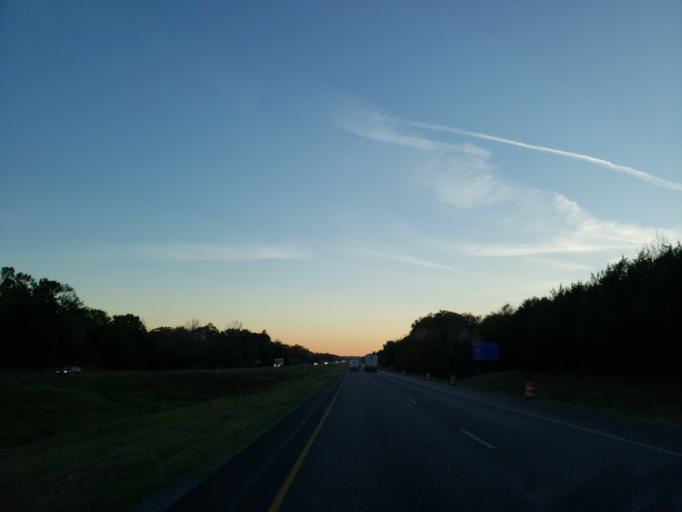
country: US
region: Alabama
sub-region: Sumter County
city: Livingston
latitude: 32.6404
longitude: -88.1999
